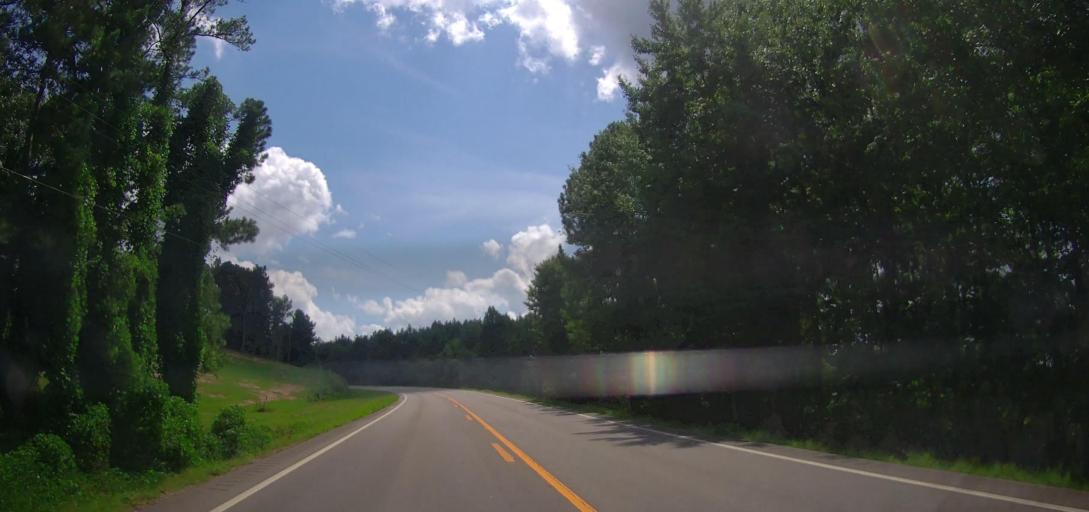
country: US
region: Alabama
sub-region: Cleburne County
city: Heflin
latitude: 33.6025
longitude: -85.4820
